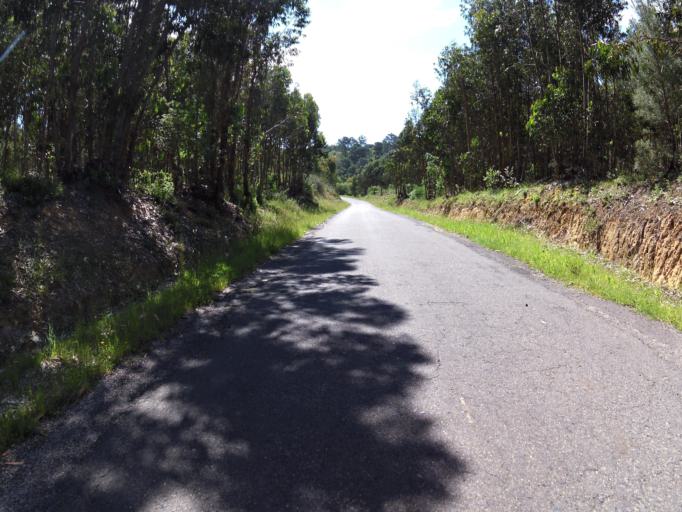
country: PT
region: Setubal
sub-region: Sines
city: Porto Covo
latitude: 37.9351
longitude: -8.7619
